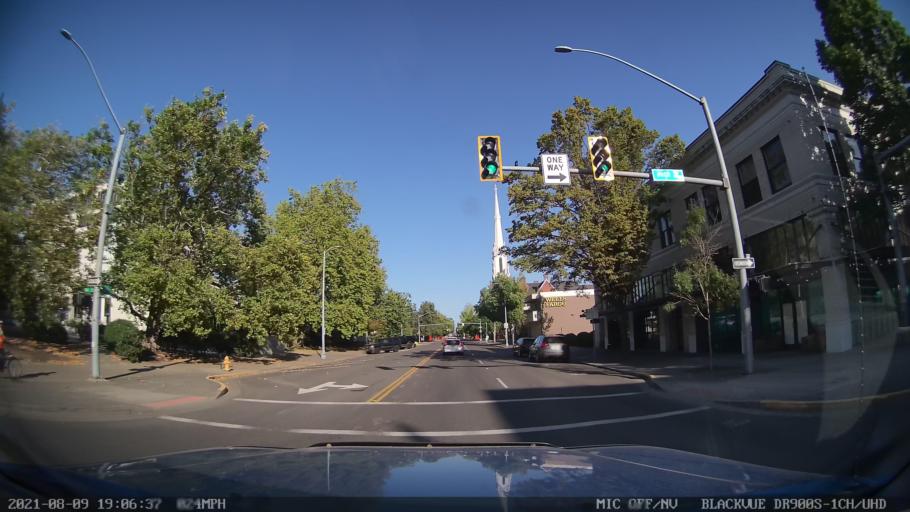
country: US
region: Oregon
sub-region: Marion County
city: Salem
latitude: 44.9395
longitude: -123.0373
